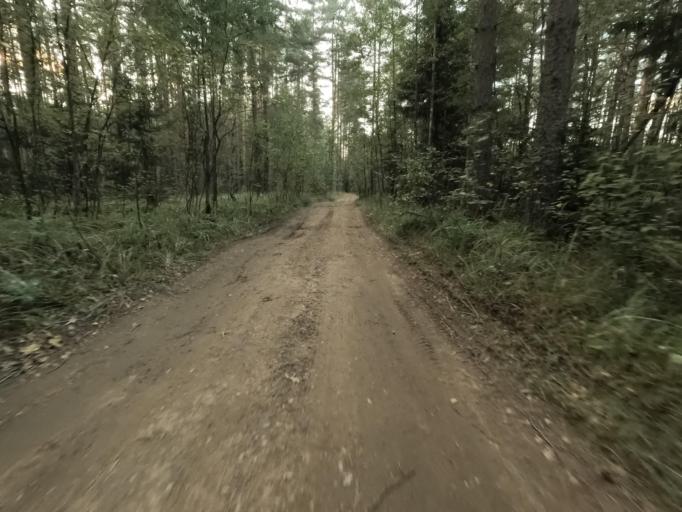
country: RU
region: Leningrad
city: Otradnoye
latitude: 59.8455
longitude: 30.7993
